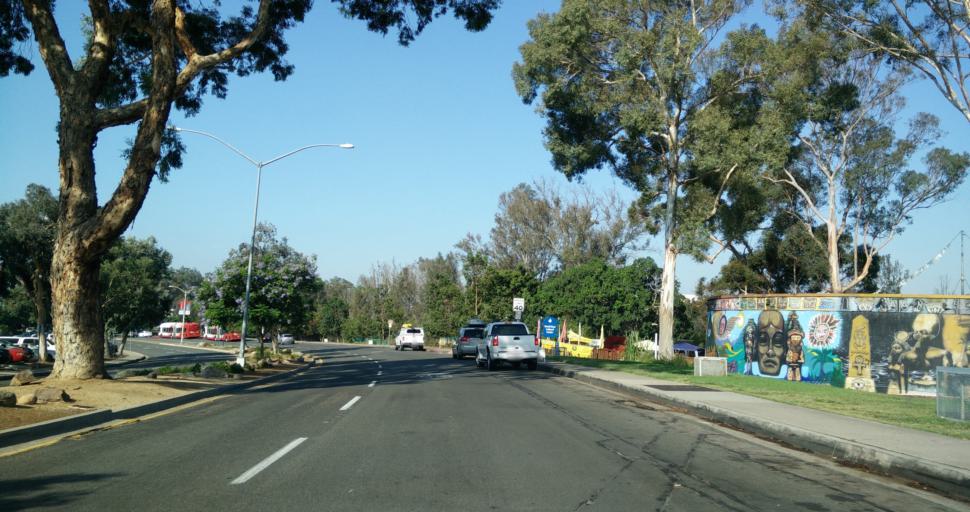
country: US
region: California
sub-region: San Diego County
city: San Diego
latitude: 32.7271
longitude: -117.1489
